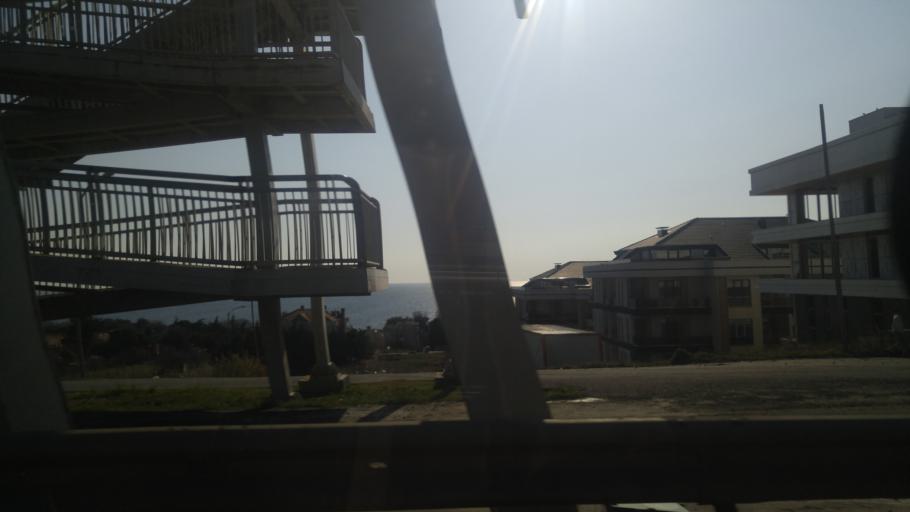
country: TR
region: Istanbul
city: Kumburgaz
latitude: 41.0160
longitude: 28.4881
